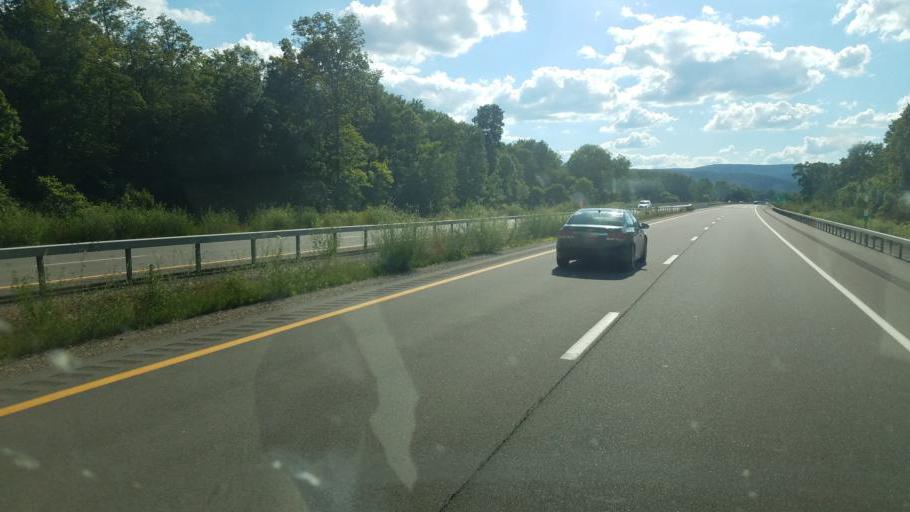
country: US
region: Pennsylvania
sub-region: McKean County
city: Foster Brook
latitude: 42.0861
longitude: -78.6155
